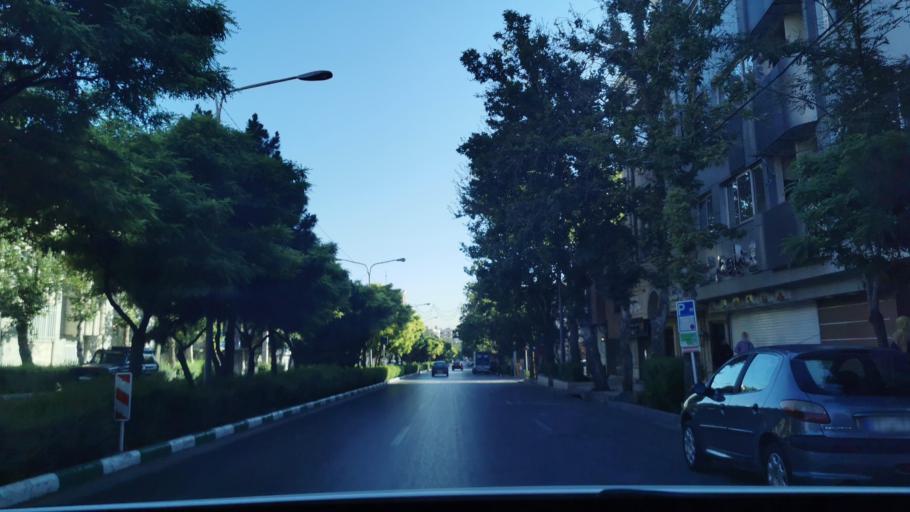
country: IR
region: Razavi Khorasan
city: Mashhad
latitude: 36.2939
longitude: 59.5681
